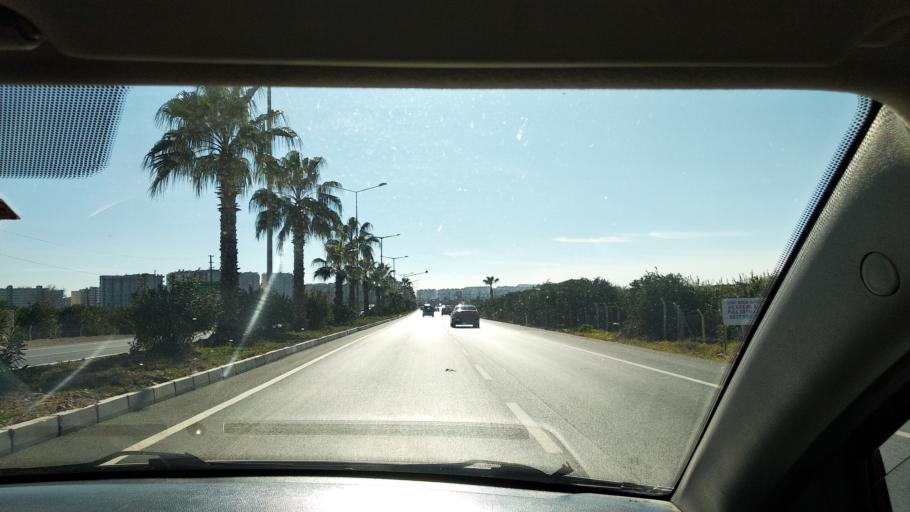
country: TR
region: Mersin
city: Tomuk
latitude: 36.6650
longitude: 34.3982
